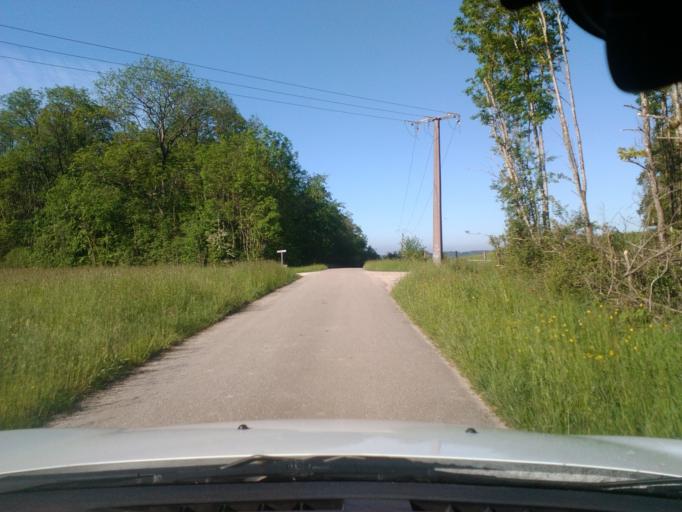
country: FR
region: Lorraine
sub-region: Departement des Vosges
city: Charmes
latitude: 48.3301
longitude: 6.2193
